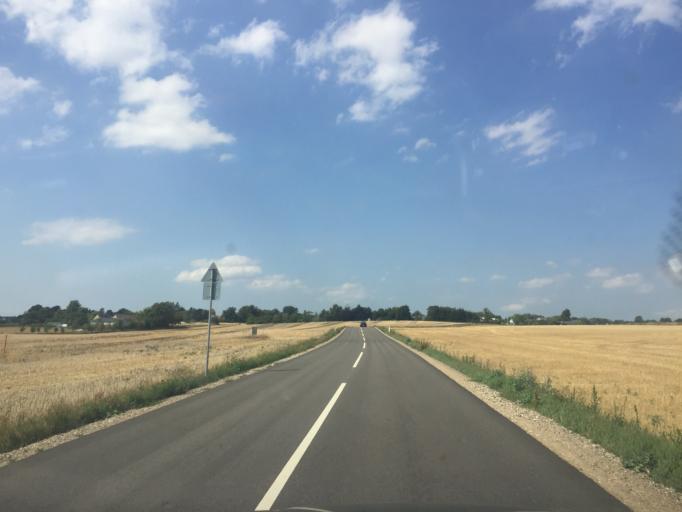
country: DK
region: Capital Region
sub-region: Egedal Kommune
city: Vekso
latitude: 55.7082
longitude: 12.2207
